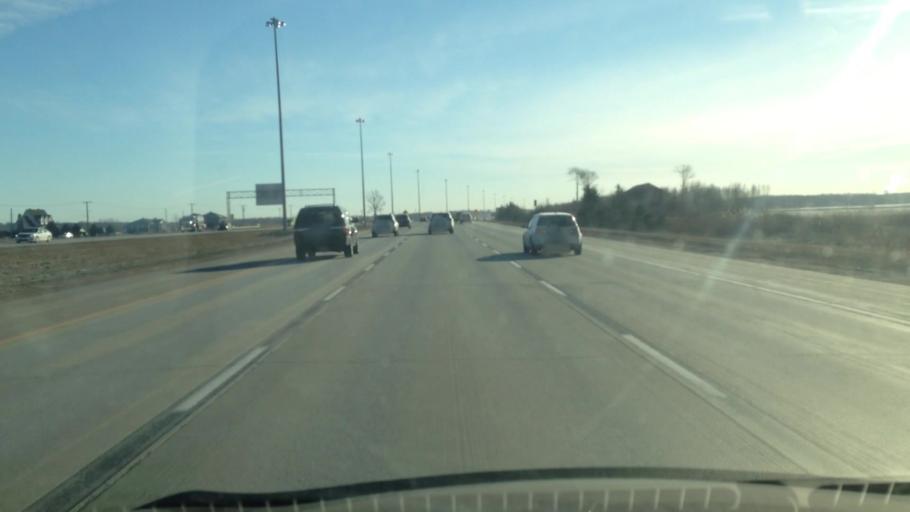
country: CA
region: Quebec
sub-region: Laurentides
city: Saint-Jerome
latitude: 45.7363
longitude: -73.9878
